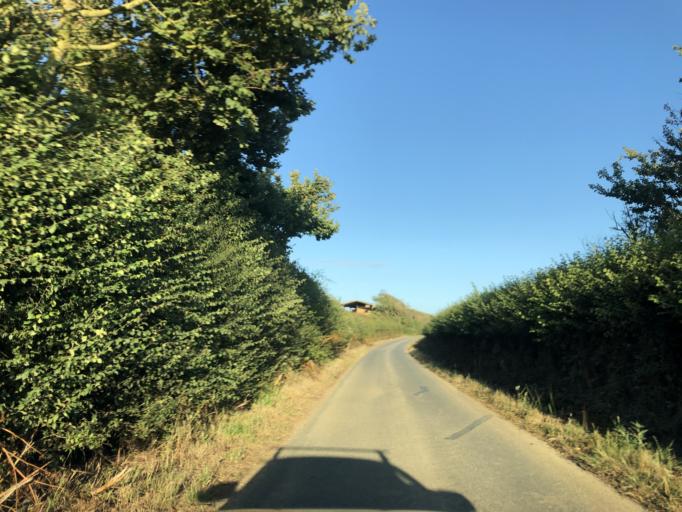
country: GB
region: England
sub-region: Isle of Wight
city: Shalfleet
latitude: 50.6359
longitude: -1.3935
